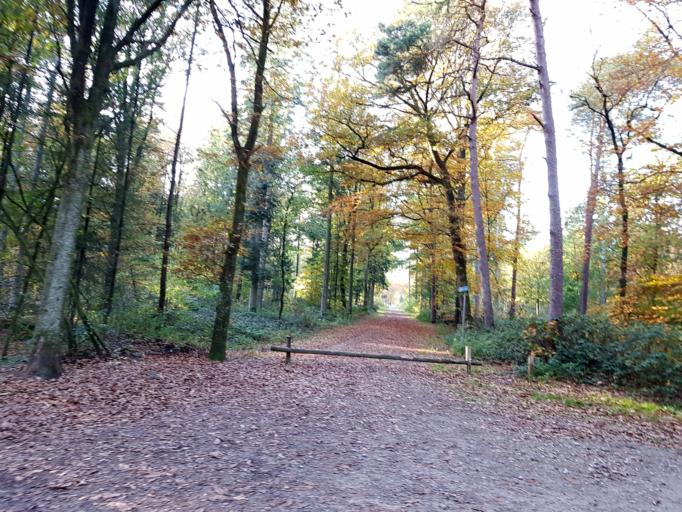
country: NL
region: Gelderland
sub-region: Gemeente Groesbeek
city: Groesbeek
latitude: 51.7798
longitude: 5.9192
